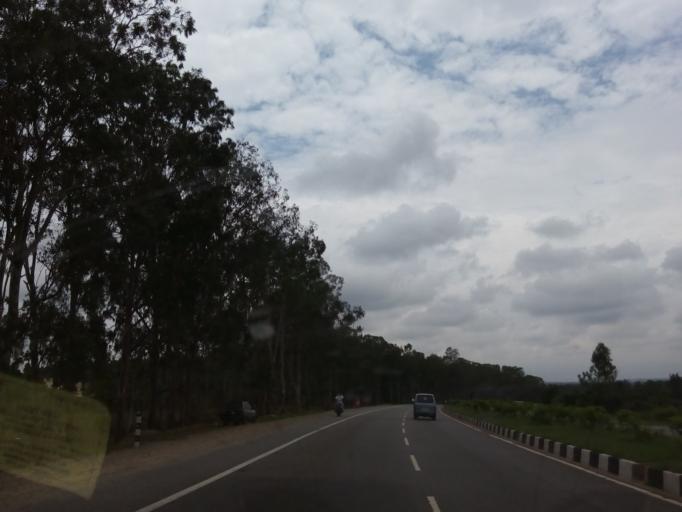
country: IN
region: Karnataka
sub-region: Hassan
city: Channarayapatna
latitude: 12.9734
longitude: 76.2686
